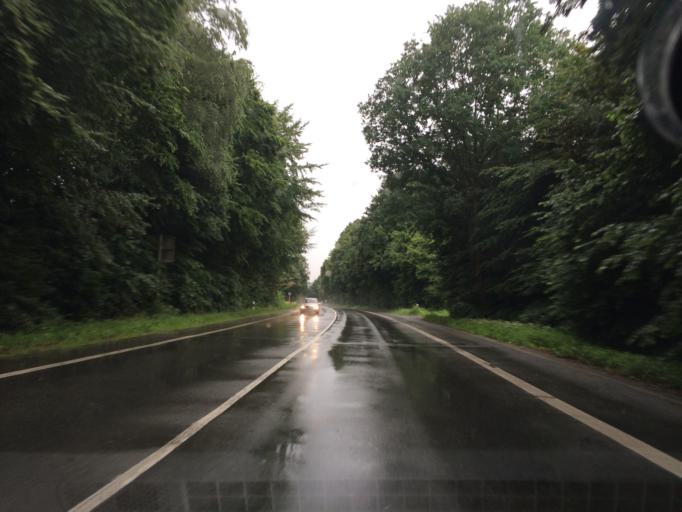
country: DE
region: North Rhine-Westphalia
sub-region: Regierungsbezirk Munster
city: Haltern
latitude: 51.7781
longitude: 7.2064
